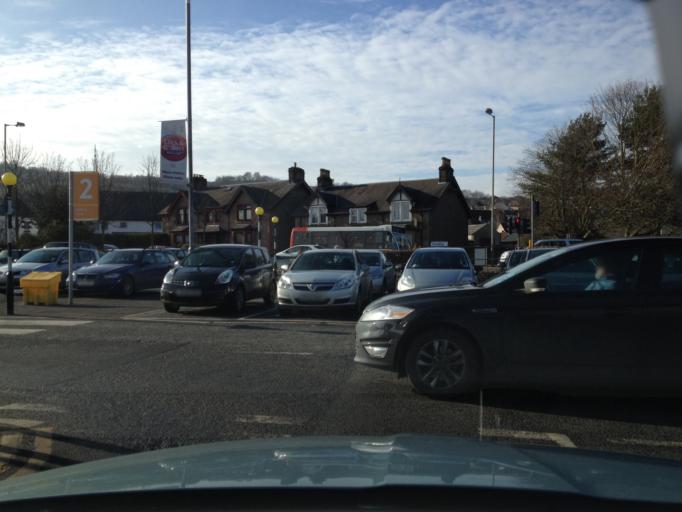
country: GB
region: Scotland
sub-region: Perth and Kinross
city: Perth
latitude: 56.3814
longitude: -3.4340
